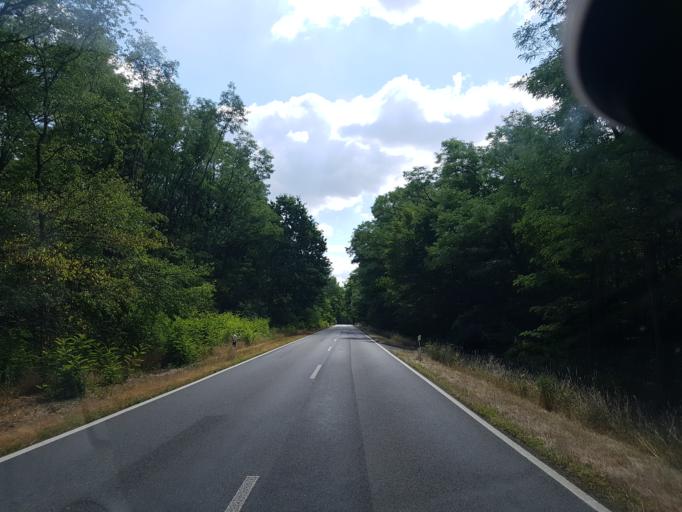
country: DE
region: Brandenburg
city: Neupetershain
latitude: 51.6854
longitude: 14.1410
